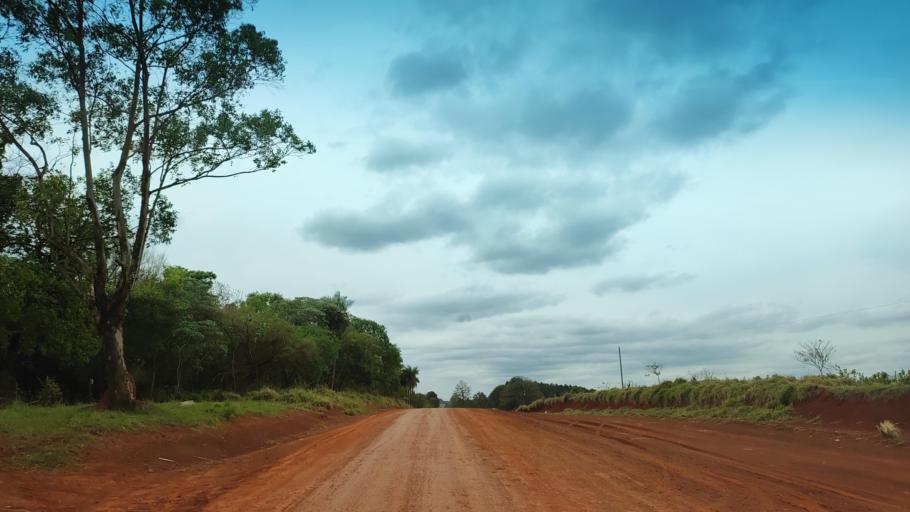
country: AR
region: Misiones
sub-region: Departamento de Capital
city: Posadas
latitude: -27.4869
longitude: -55.9708
